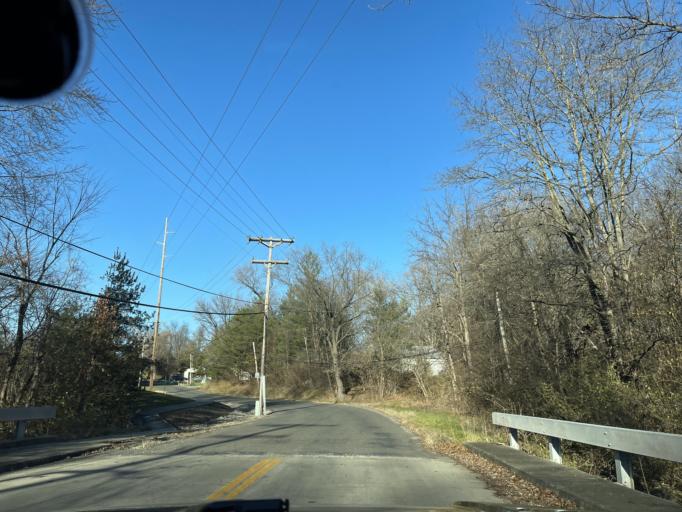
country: US
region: Illinois
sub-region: Sangamon County
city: Leland Grove
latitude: 39.8016
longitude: -89.7158
